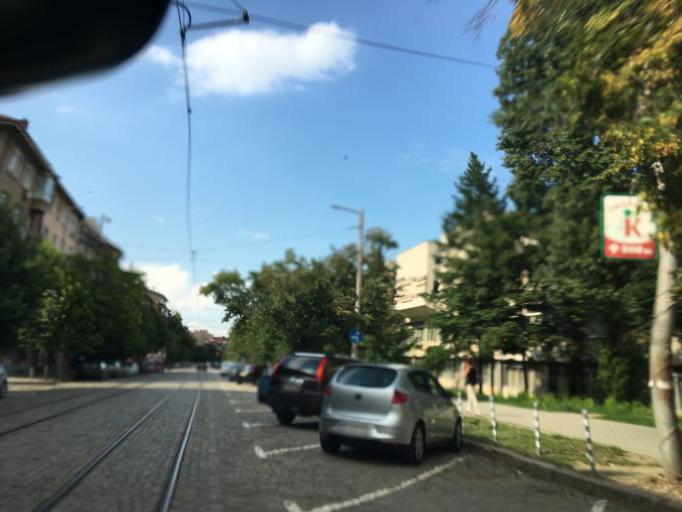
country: BG
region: Sofia-Capital
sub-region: Stolichna Obshtina
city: Sofia
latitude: 42.6830
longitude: 23.3312
